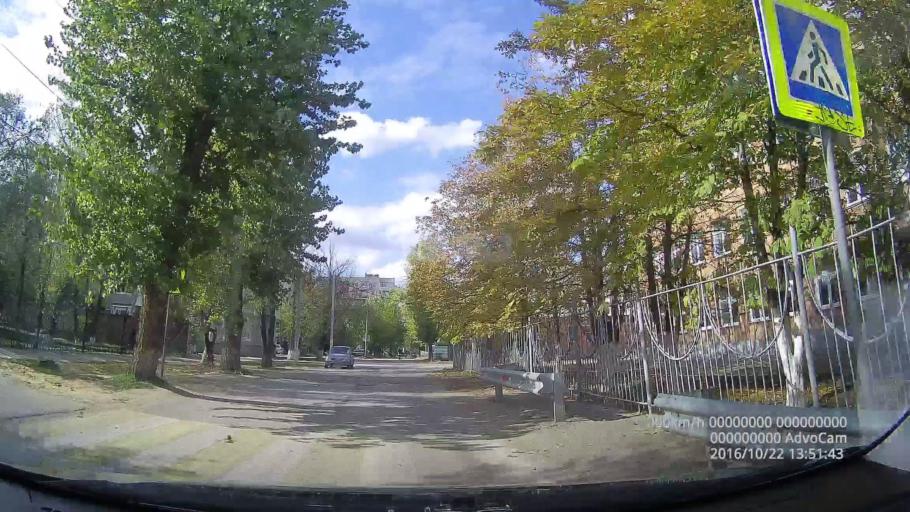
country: RU
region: Rostov
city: Kamensk-Shakhtinskiy
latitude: 48.3145
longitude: 40.2632
